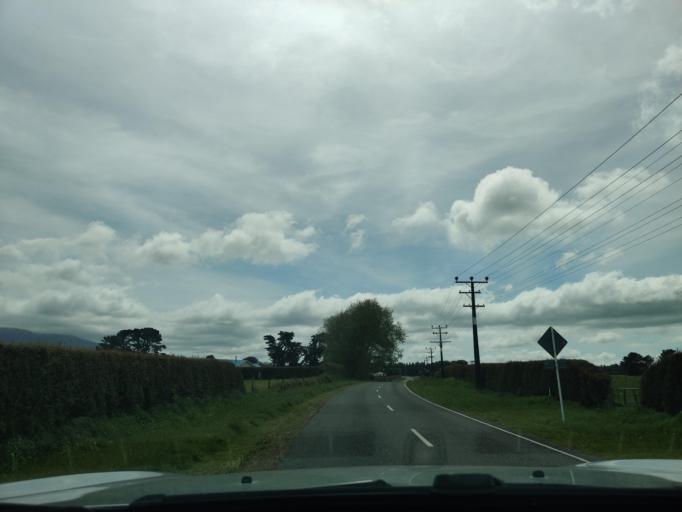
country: NZ
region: Taranaki
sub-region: South Taranaki District
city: Eltham
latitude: -39.3844
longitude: 174.1452
